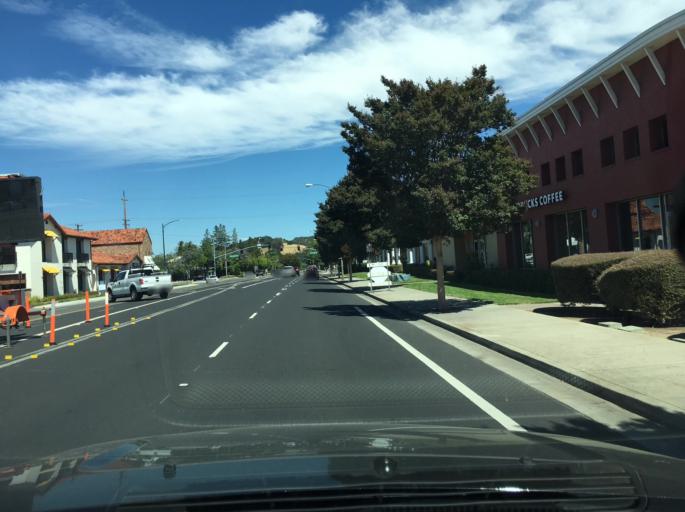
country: US
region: California
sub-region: Santa Clara County
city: Los Gatos
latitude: 37.2359
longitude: -121.9647
